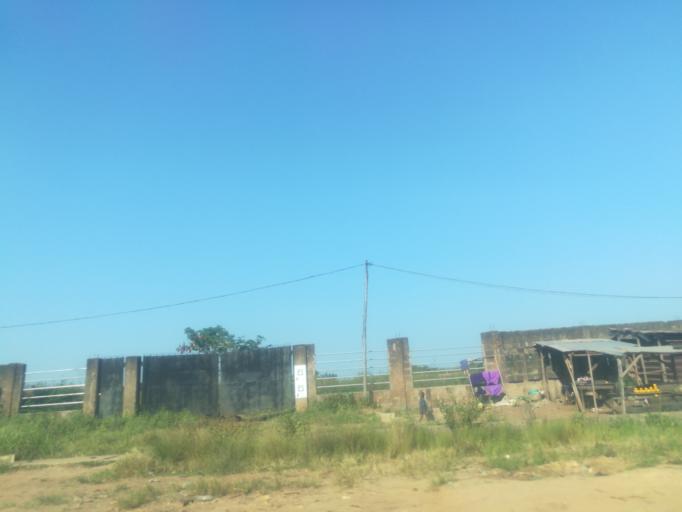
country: NG
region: Ogun
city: Abeokuta
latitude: 7.1769
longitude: 3.2872
